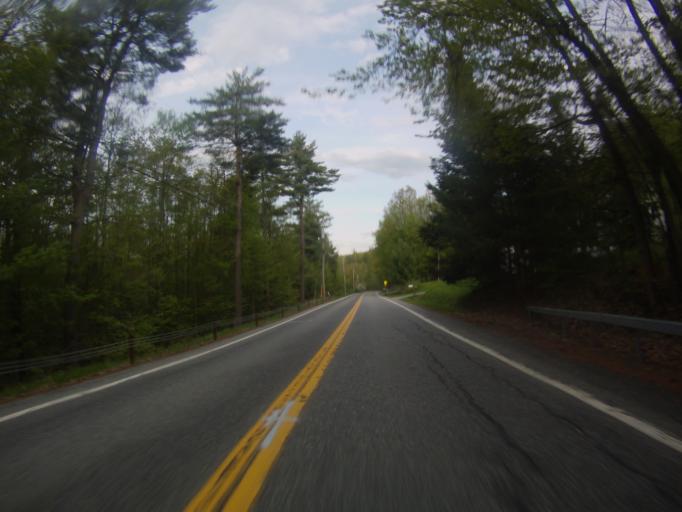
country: US
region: New York
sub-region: Essex County
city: Ticonderoga
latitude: 43.7585
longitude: -73.5330
